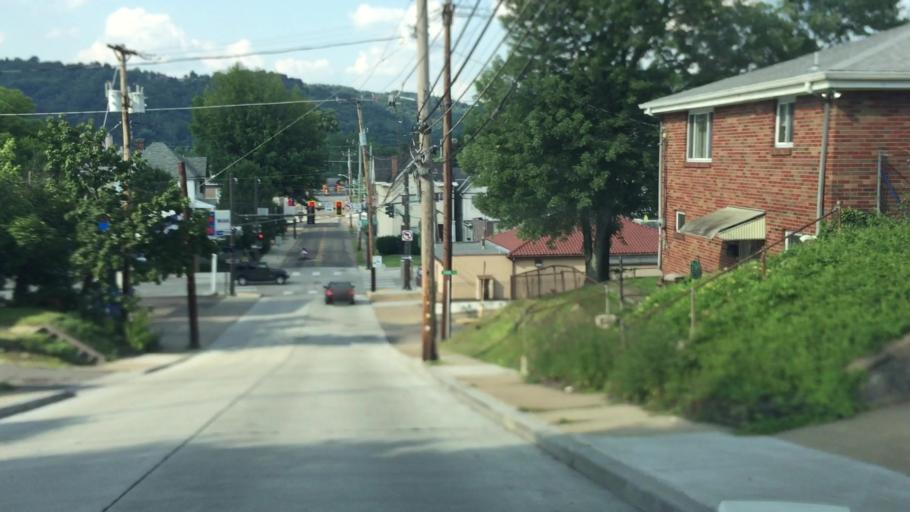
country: US
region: Pennsylvania
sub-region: Allegheny County
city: Coraopolis
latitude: 40.5178
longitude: -80.1672
